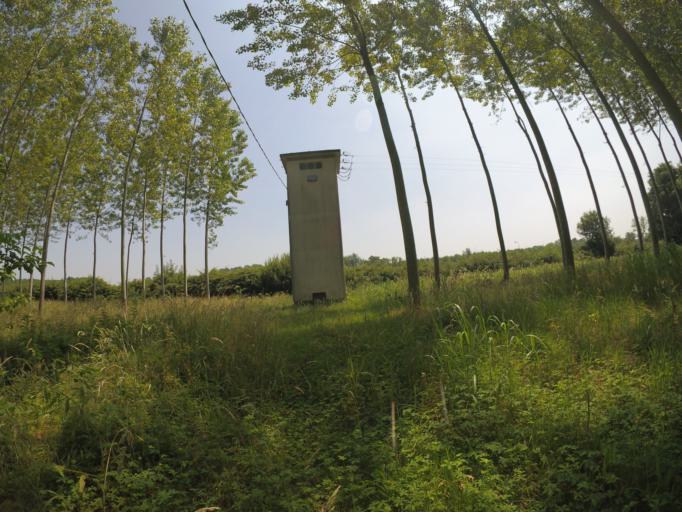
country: IT
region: Friuli Venezia Giulia
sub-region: Provincia di Udine
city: Bertiolo
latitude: 45.9143
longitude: 13.0576
